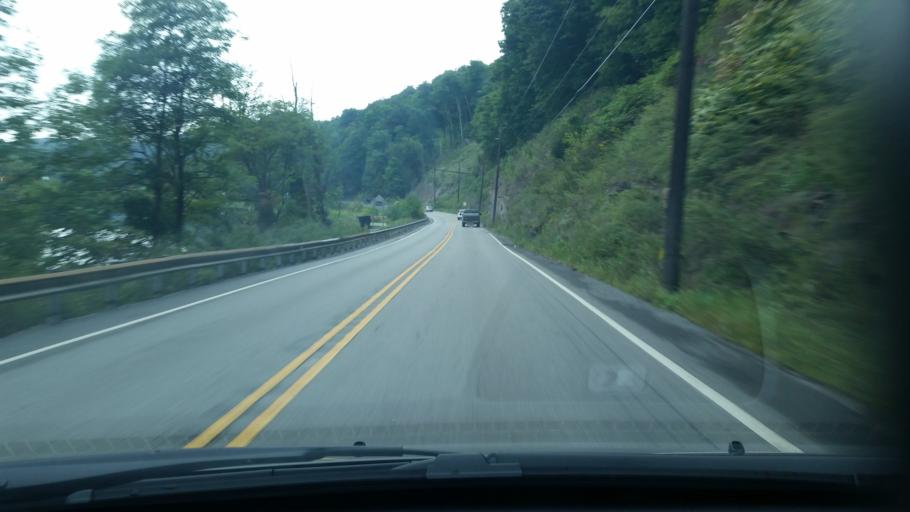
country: US
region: Pennsylvania
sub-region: Clearfield County
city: Shiloh
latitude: 41.0693
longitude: -78.3660
